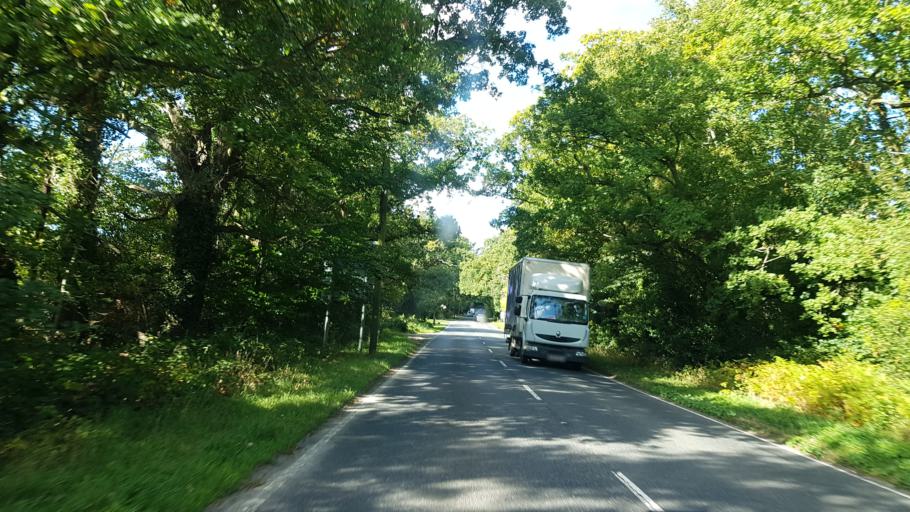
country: GB
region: England
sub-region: Surrey
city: Chiddingfold
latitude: 51.0781
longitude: -0.6484
